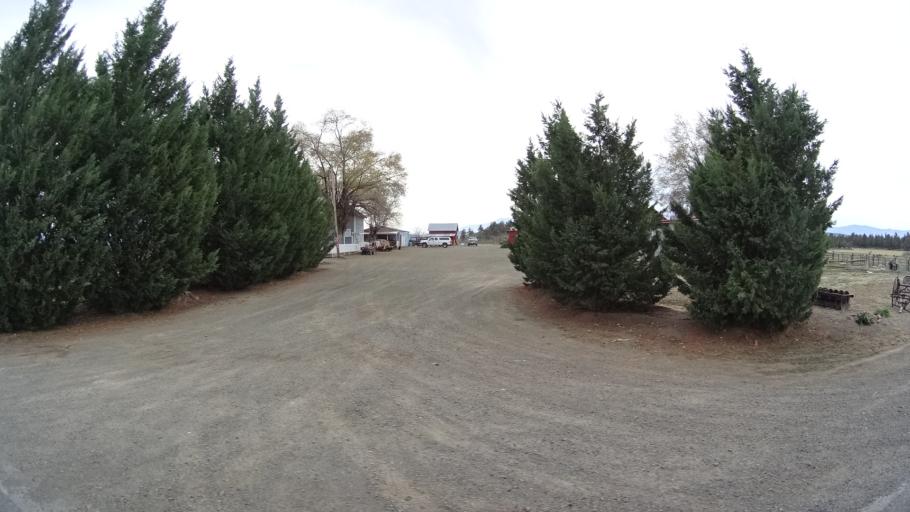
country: US
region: California
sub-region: Siskiyou County
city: Montague
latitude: 41.6241
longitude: -122.4132
